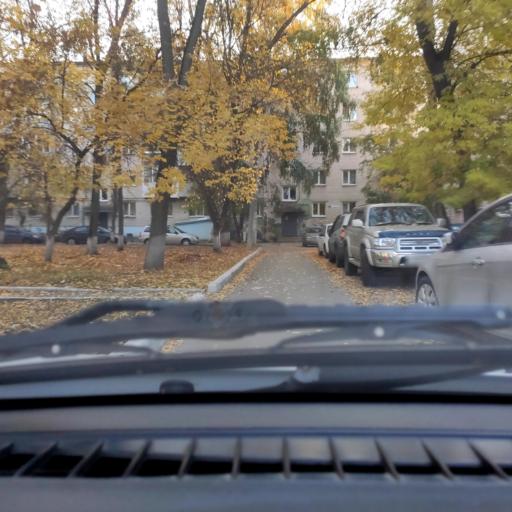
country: RU
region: Samara
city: Tol'yatti
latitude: 53.4999
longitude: 49.4083
